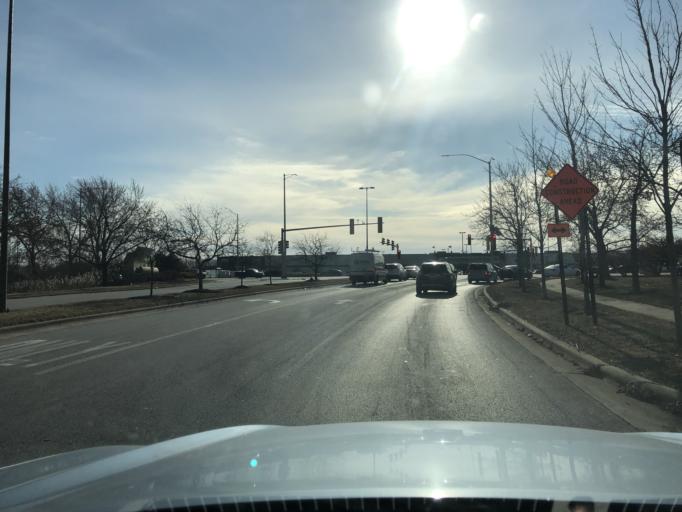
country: US
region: Illinois
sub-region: Lake County
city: Grandwood Park
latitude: 42.3856
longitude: -87.9603
